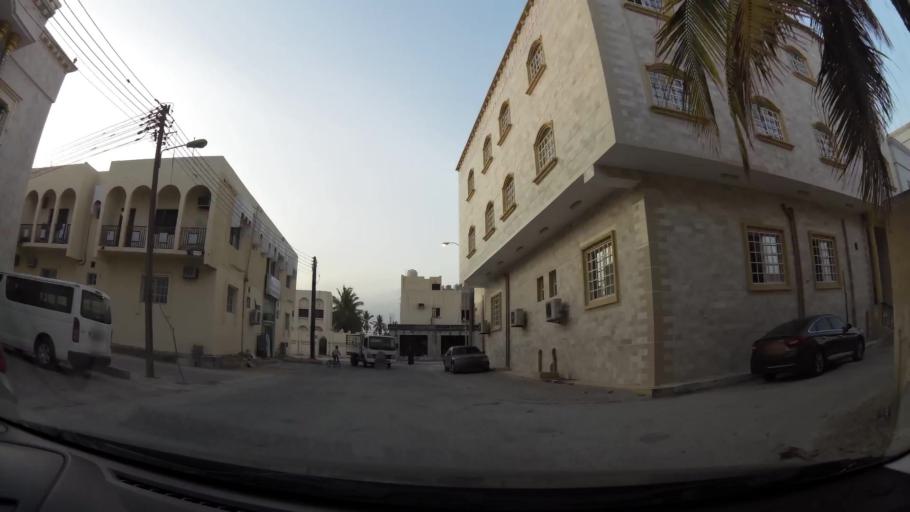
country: OM
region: Zufar
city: Salalah
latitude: 17.0209
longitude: 54.1259
